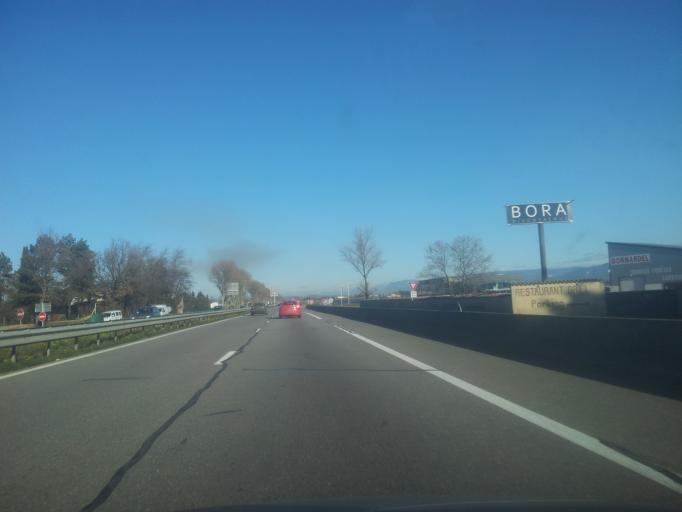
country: FR
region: Rhone-Alpes
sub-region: Departement de la Drome
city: Alixan
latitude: 44.9996
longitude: 5.0015
